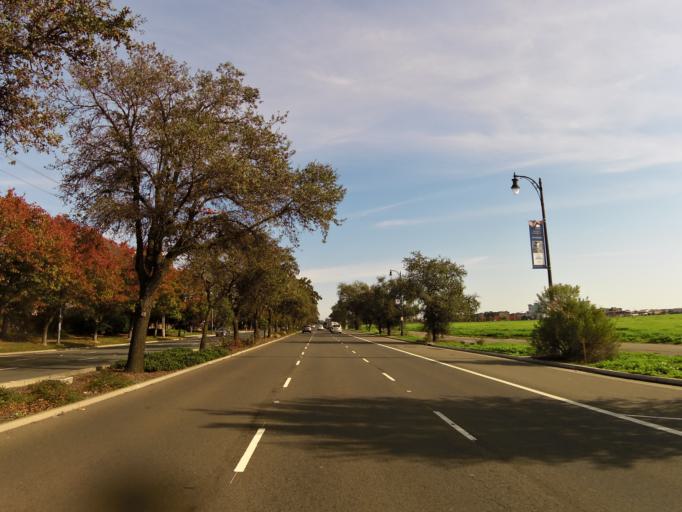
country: US
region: California
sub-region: Sacramento County
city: Laguna
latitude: 38.4089
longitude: -121.4156
